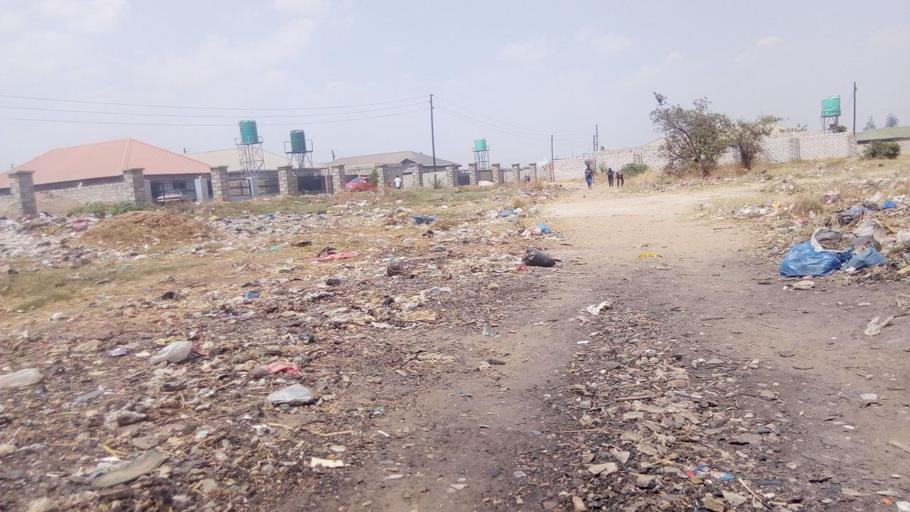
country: ZM
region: Lusaka
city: Lusaka
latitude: -15.3663
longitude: 28.2901
